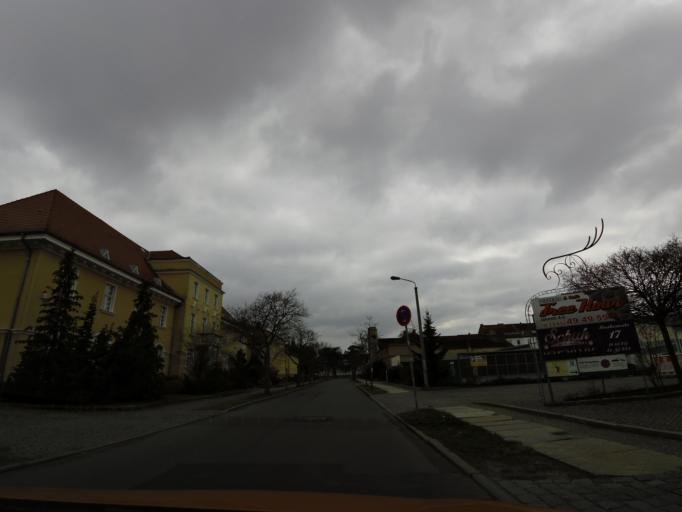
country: DE
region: Brandenburg
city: Rathenow
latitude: 52.6102
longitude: 12.3487
